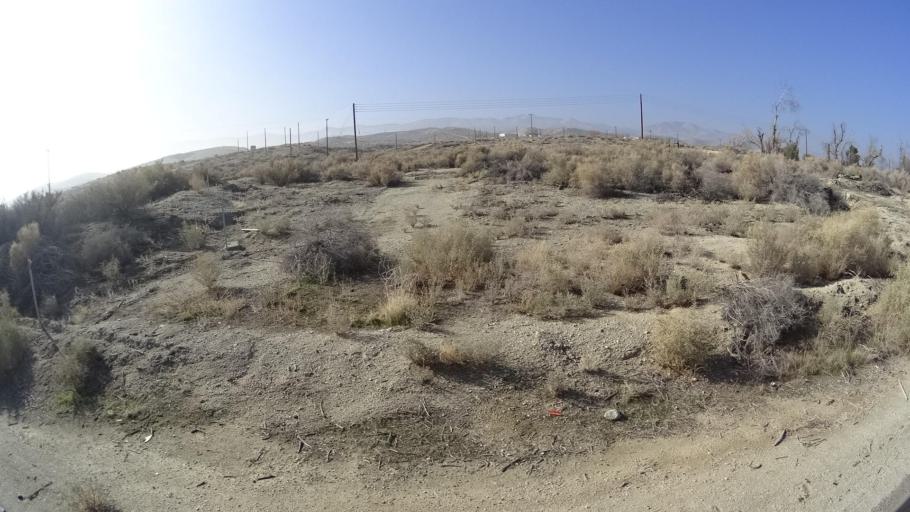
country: US
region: California
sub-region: Kern County
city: Taft Heights
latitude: 35.1744
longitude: -119.5381
